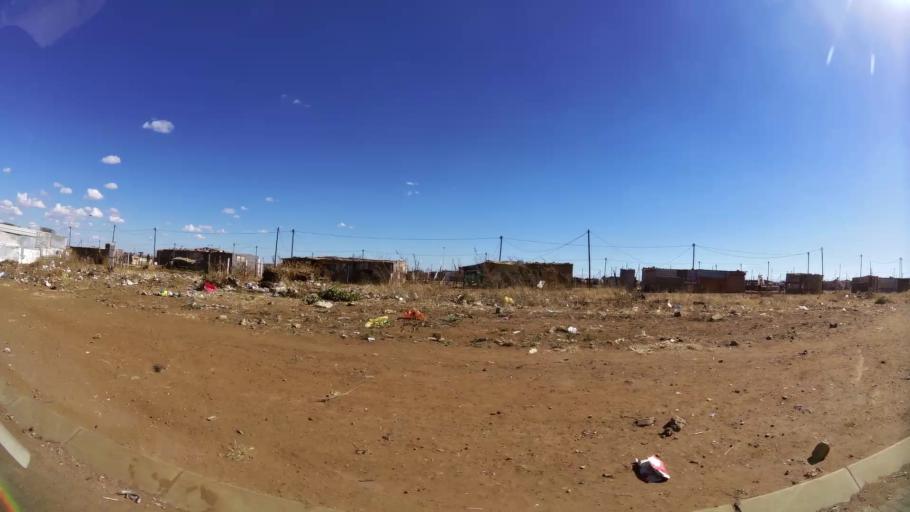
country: ZA
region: North-West
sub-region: Dr Kenneth Kaunda District Municipality
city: Klerksdorp
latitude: -26.8693
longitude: 26.5650
